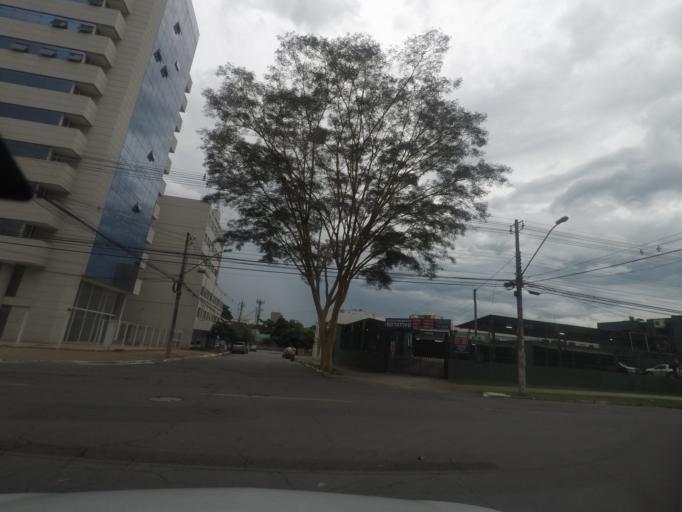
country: BR
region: Goias
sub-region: Goiania
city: Goiania
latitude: -16.6792
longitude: -49.2683
